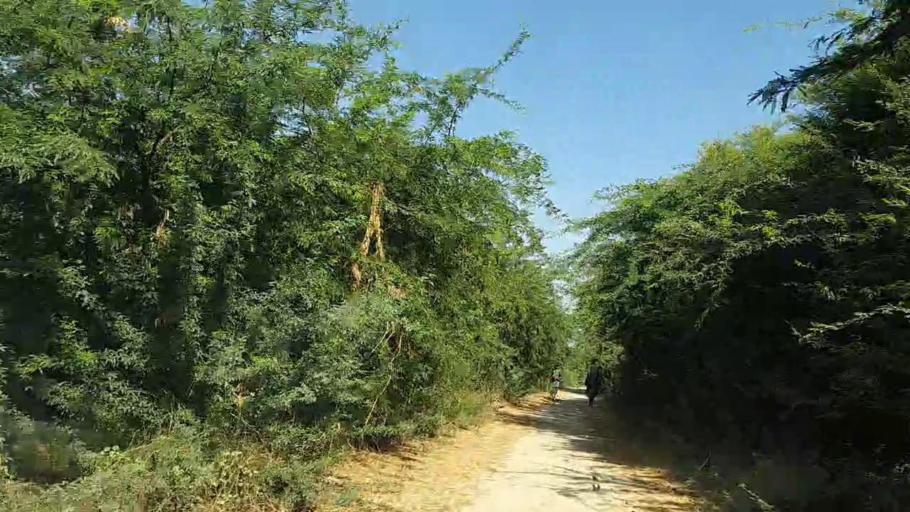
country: PK
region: Sindh
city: Daro Mehar
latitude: 24.8086
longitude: 68.1838
